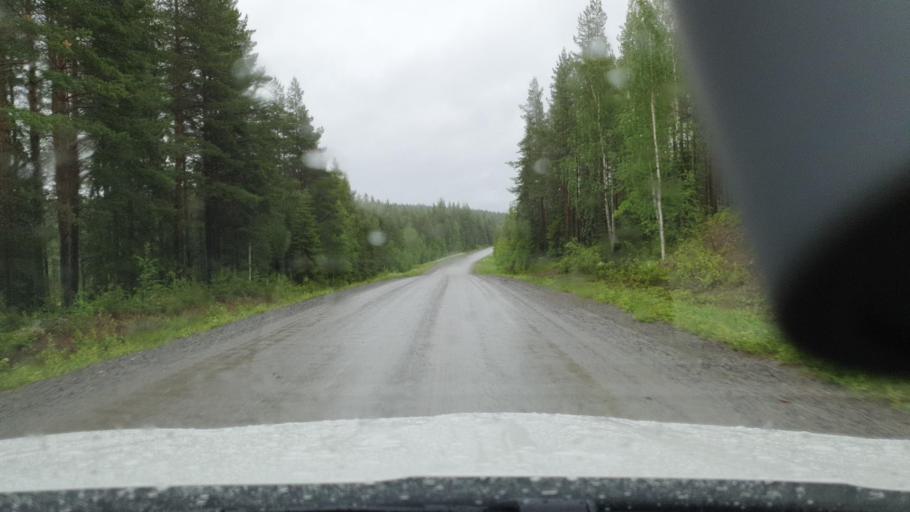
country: SE
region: Vaesterbotten
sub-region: Skelleftea Kommun
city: Burtraesk
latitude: 64.3799
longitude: 20.3406
